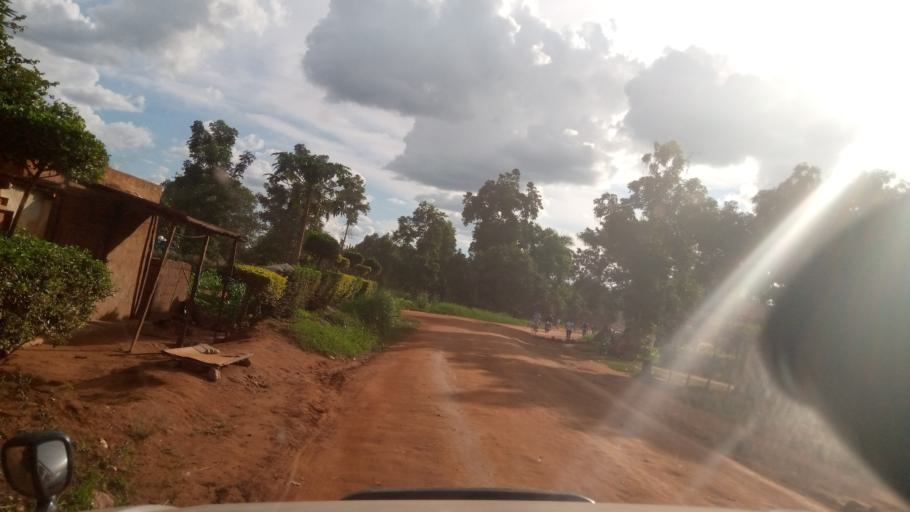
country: UG
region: Northern Region
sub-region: Lira District
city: Lira
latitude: 2.2275
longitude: 32.8978
